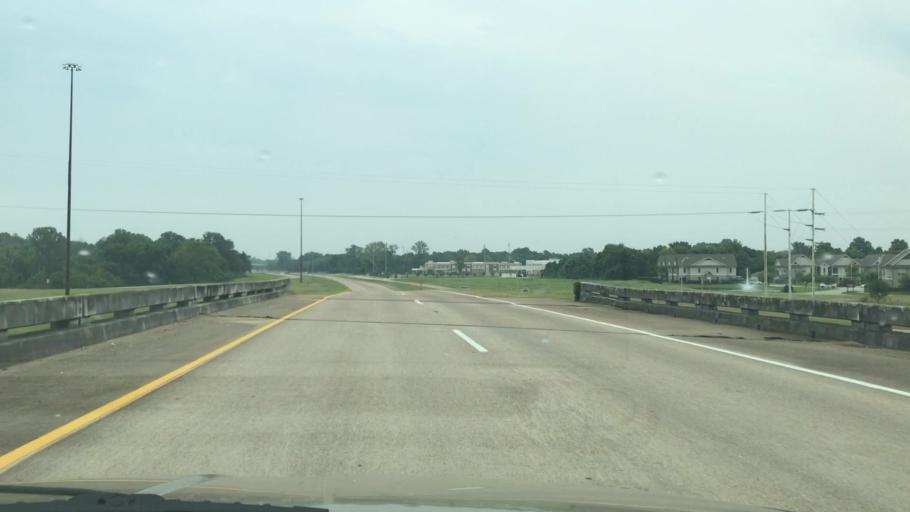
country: US
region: Louisiana
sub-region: Bossier Parish
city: Bossier City
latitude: 32.5002
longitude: -93.7157
